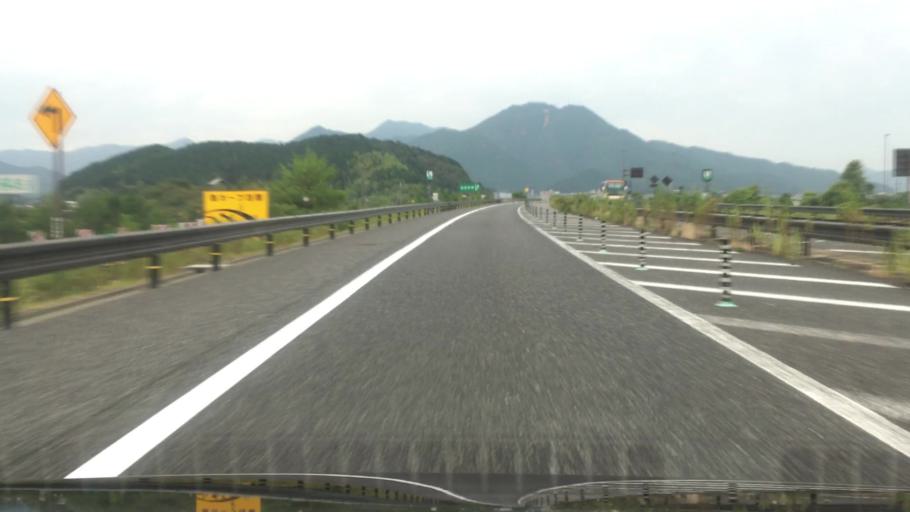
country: JP
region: Kyoto
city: Fukuchiyama
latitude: 35.1621
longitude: 135.0464
